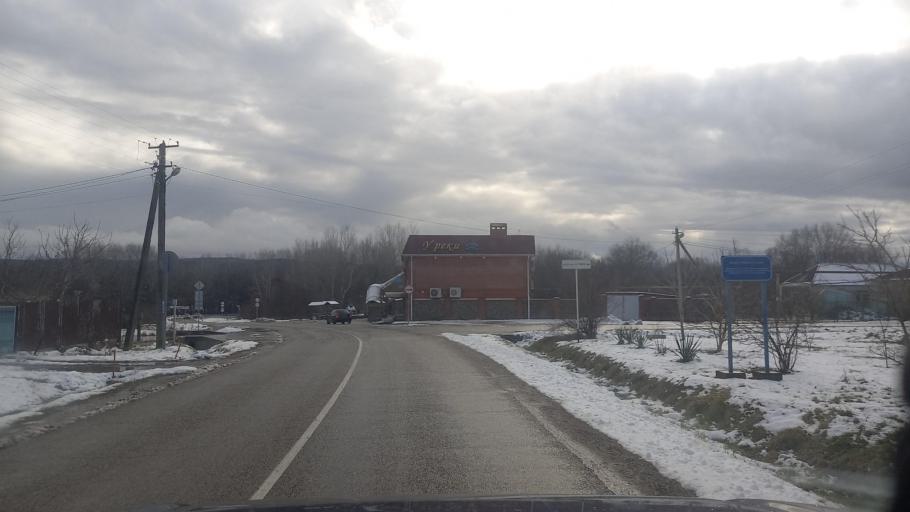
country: RU
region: Krasnodarskiy
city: Smolenskaya
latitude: 44.7738
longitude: 38.8458
